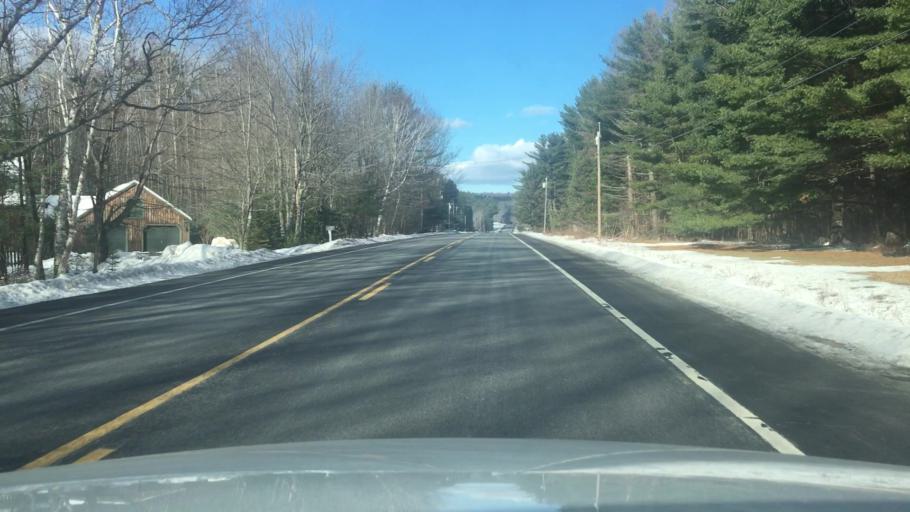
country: US
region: Maine
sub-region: Somerset County
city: Madison
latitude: 44.8512
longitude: -69.7917
